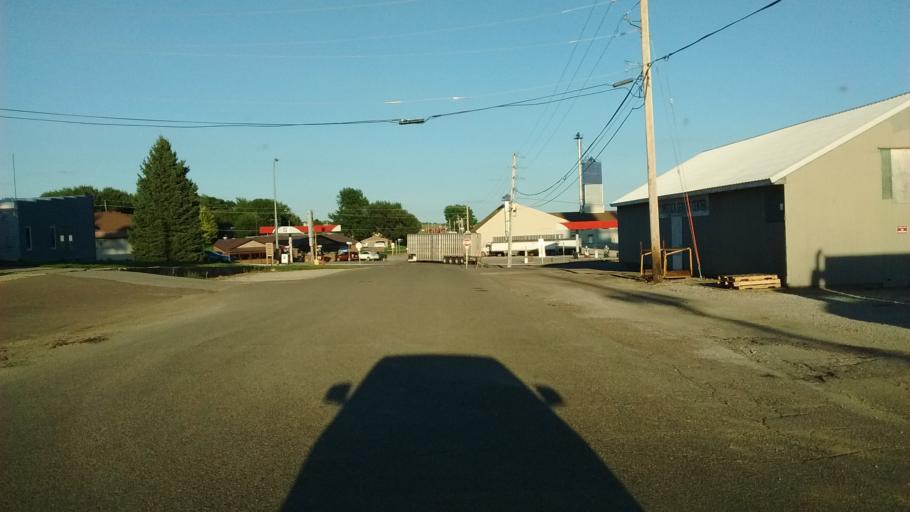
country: US
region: Iowa
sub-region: Plymouth County
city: Kingsley
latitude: 42.5869
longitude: -95.9685
